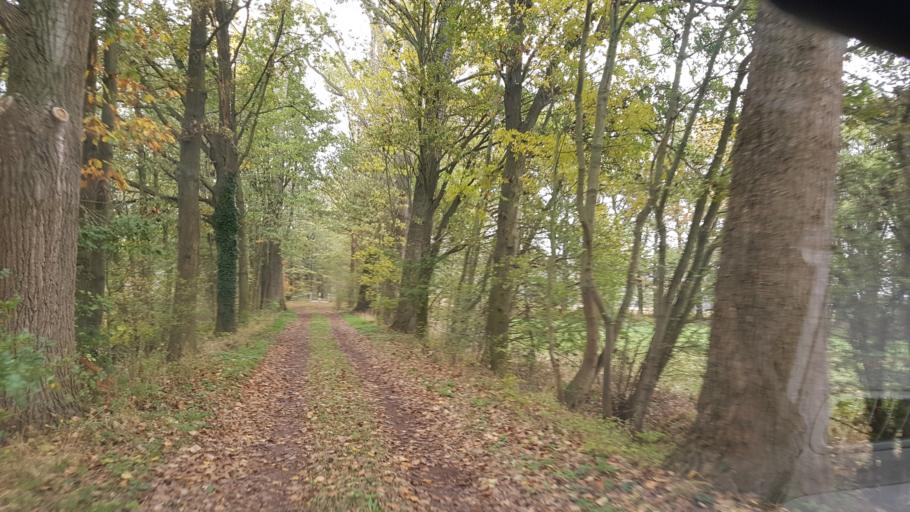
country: DE
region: Brandenburg
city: Schonewalde
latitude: 51.6932
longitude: 13.5990
